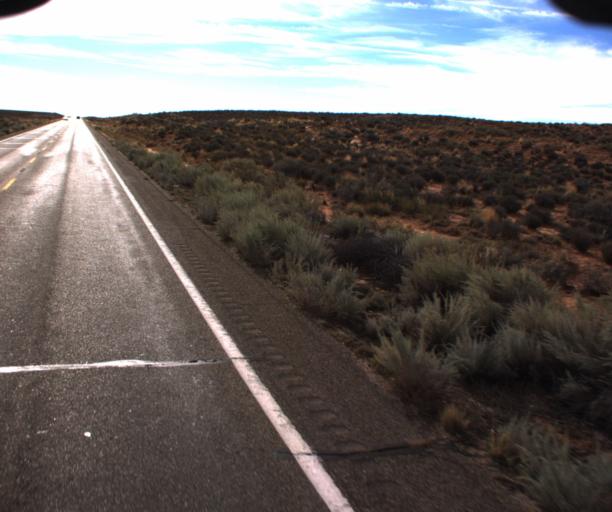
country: US
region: Arizona
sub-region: Coconino County
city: LeChee
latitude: 36.8364
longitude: -111.3203
